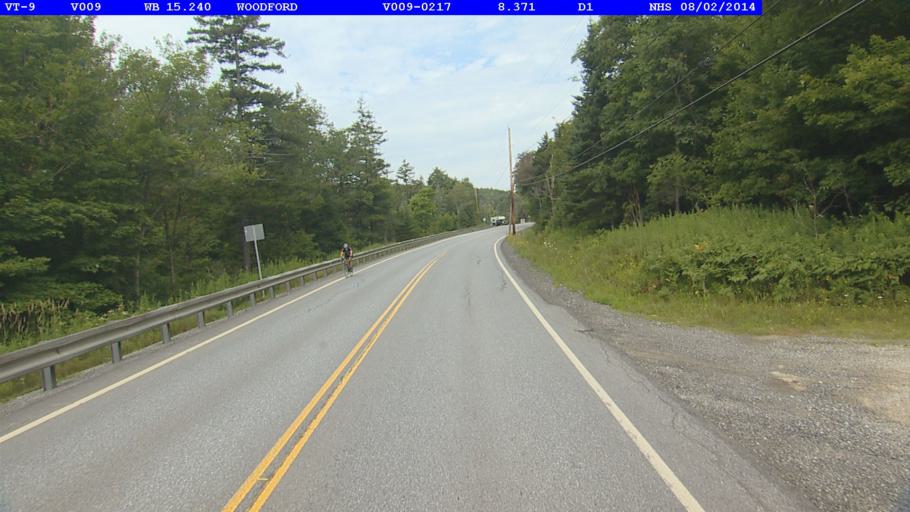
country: US
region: Vermont
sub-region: Bennington County
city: Bennington
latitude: 42.8913
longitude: -73.0334
